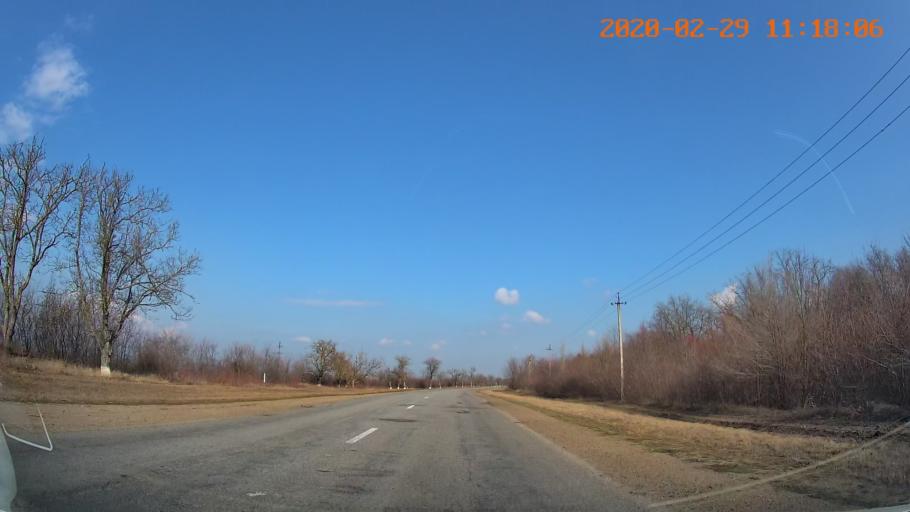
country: MD
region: Telenesti
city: Dubasari
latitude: 47.3304
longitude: 29.1720
